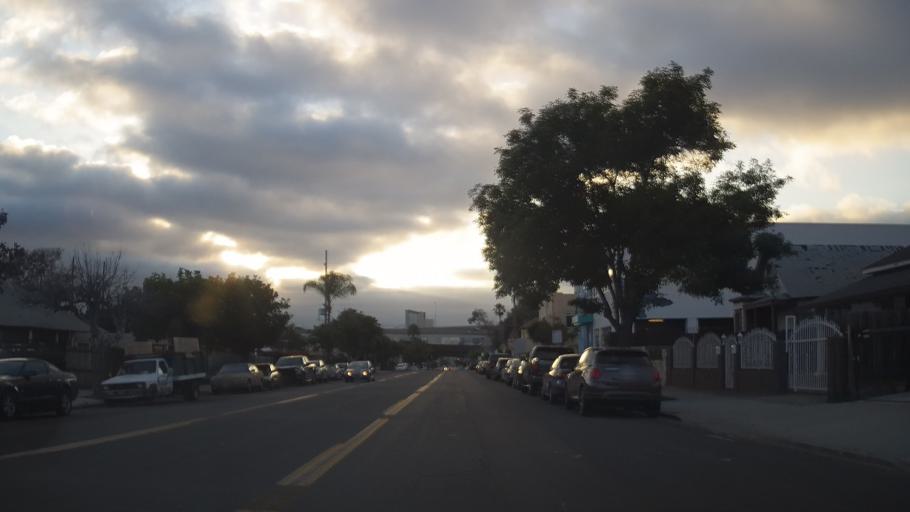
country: US
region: California
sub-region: San Diego County
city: San Diego
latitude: 32.6977
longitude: -117.1407
